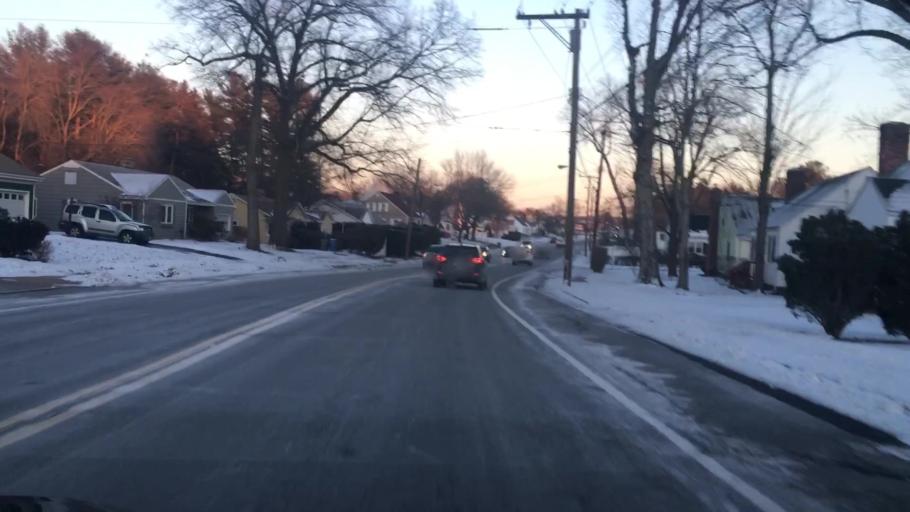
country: US
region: Connecticut
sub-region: Hartford County
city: Manchester
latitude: 41.7814
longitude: -72.5561
